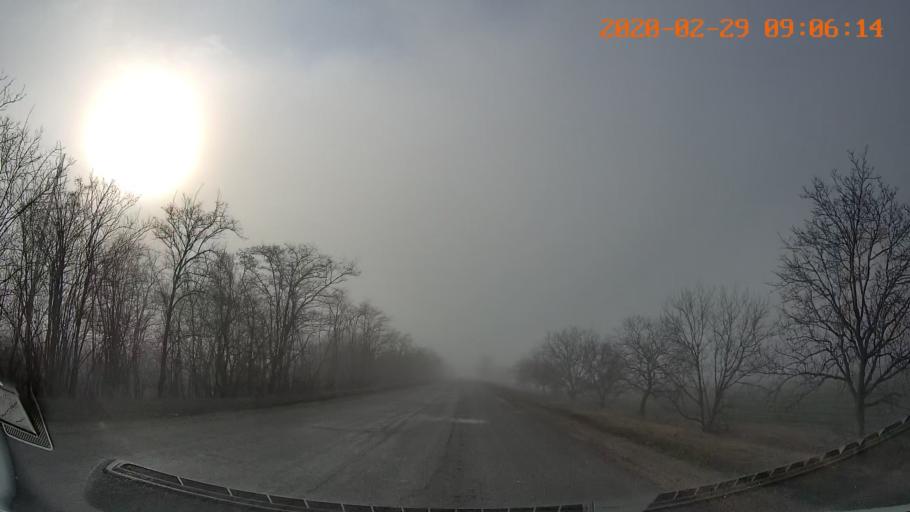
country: MD
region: Telenesti
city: Tiraspolul Nou
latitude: 46.8784
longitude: 29.7437
